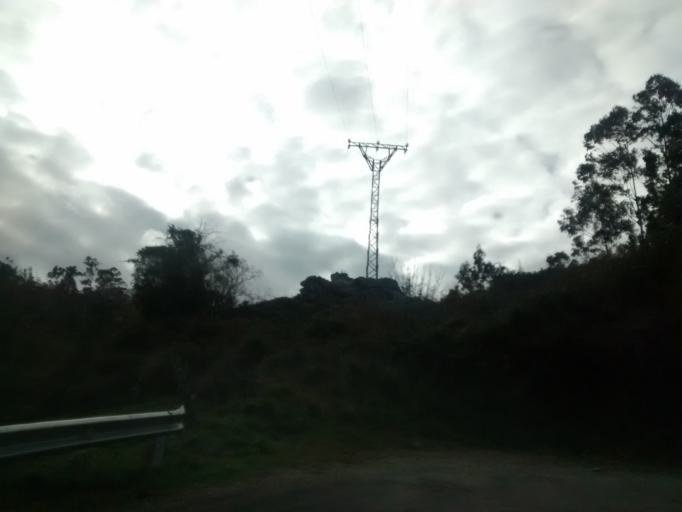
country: ES
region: Cantabria
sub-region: Provincia de Cantabria
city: Lierganes
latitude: 43.3337
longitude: -3.7040
